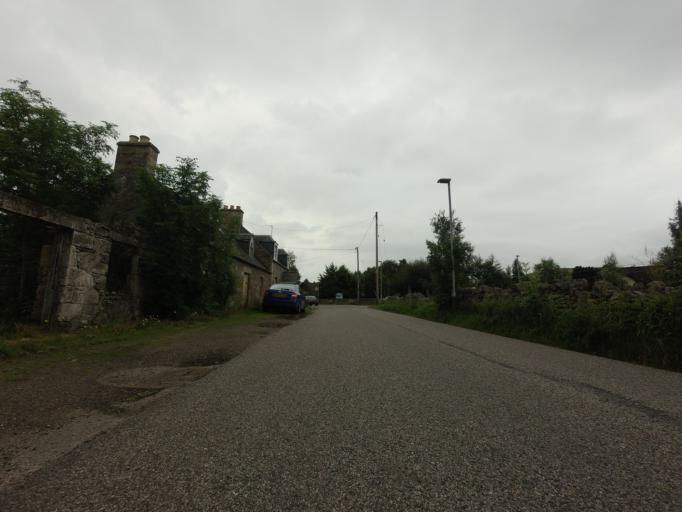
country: GB
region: Scotland
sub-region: Highland
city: Evanton
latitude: 57.8855
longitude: -4.3797
